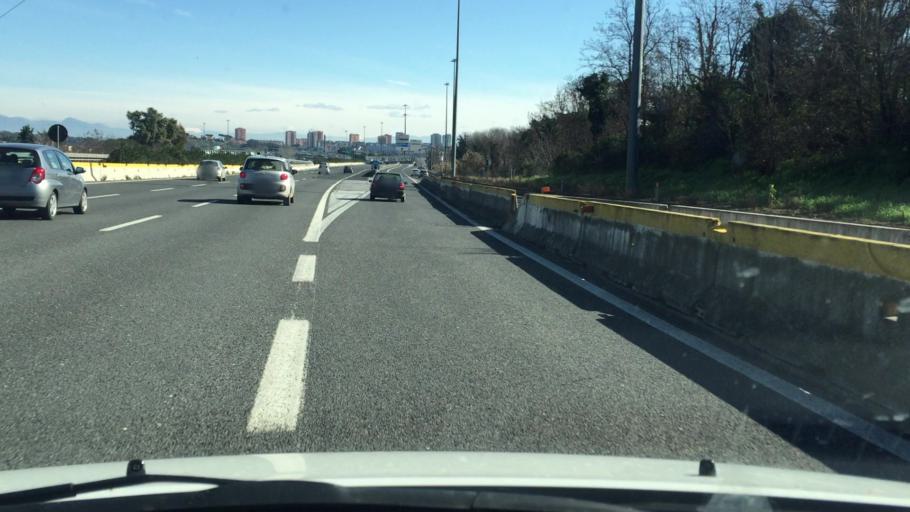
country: IT
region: Latium
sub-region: Citta metropolitana di Roma Capitale
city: Monte Caminetto
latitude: 41.9862
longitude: 12.4823
